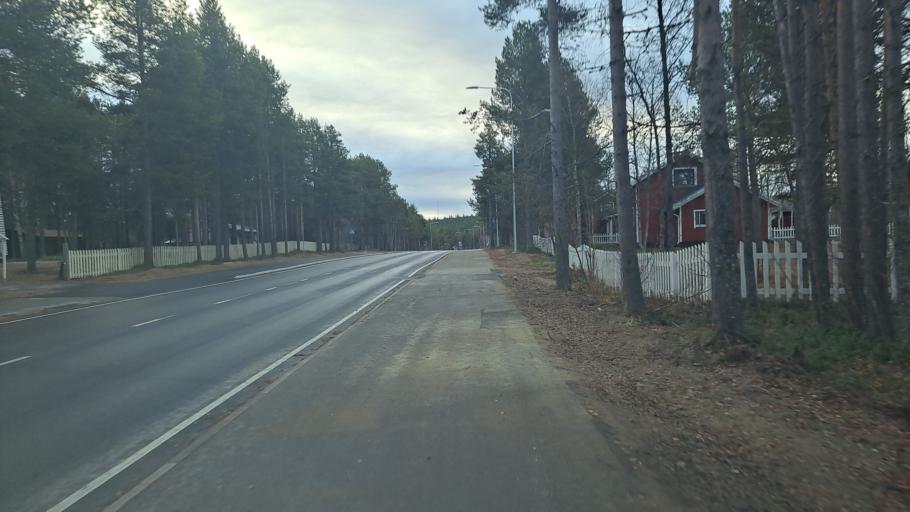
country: FI
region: Lapland
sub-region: Pohjois-Lappi
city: Inari
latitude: 68.9051
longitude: 27.0304
